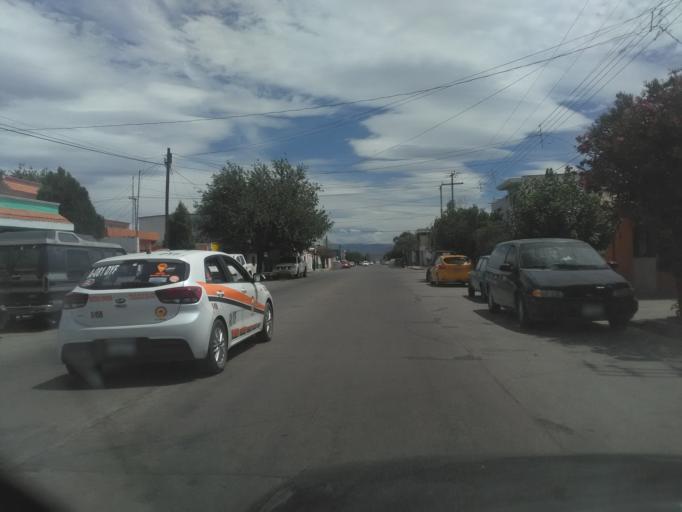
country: MX
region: Durango
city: Victoria de Durango
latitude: 24.0255
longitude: -104.6313
